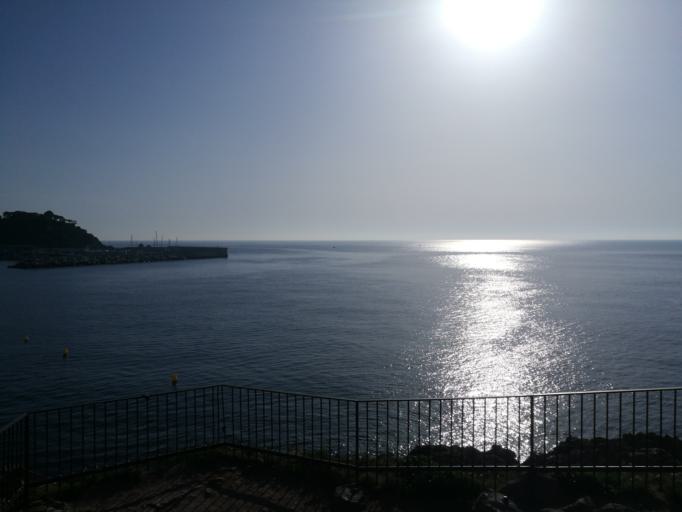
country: ES
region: Catalonia
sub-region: Provincia de Girona
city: Blanes
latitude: 41.6706
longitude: 2.7919
